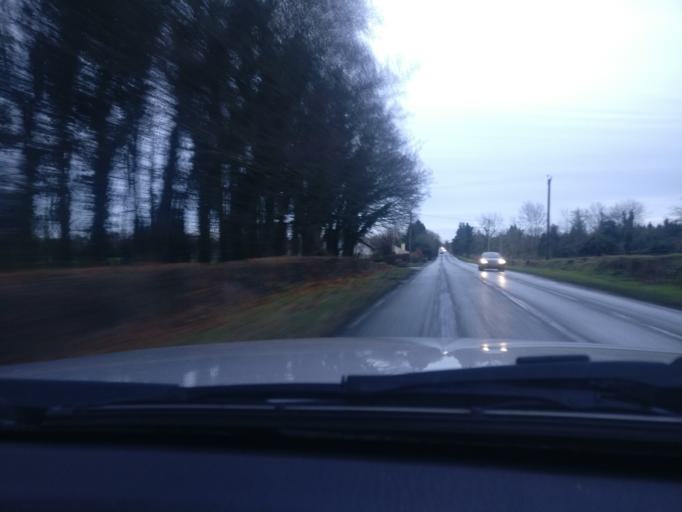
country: IE
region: Leinster
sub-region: An Mhi
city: Navan
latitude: 53.6793
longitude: -6.7537
